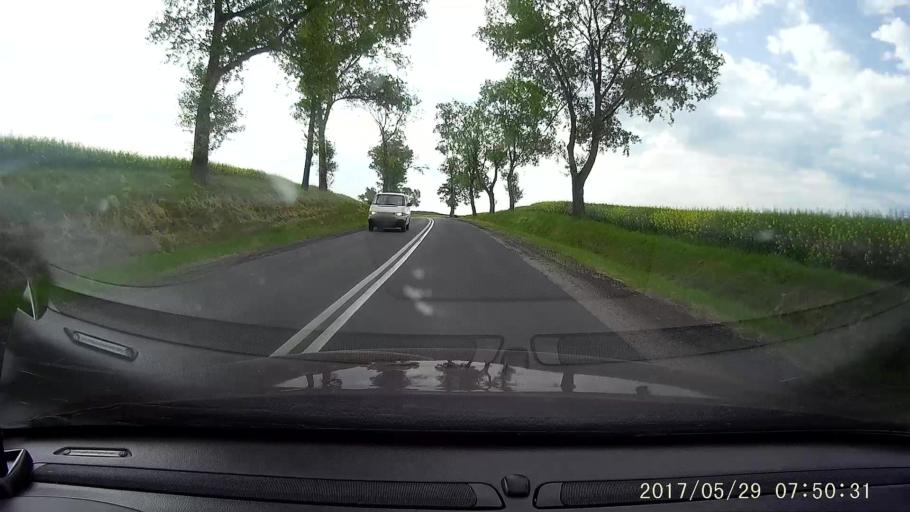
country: PL
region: Lower Silesian Voivodeship
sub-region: Powiat zlotoryjski
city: Olszanica
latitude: 51.2241
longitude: 15.6944
